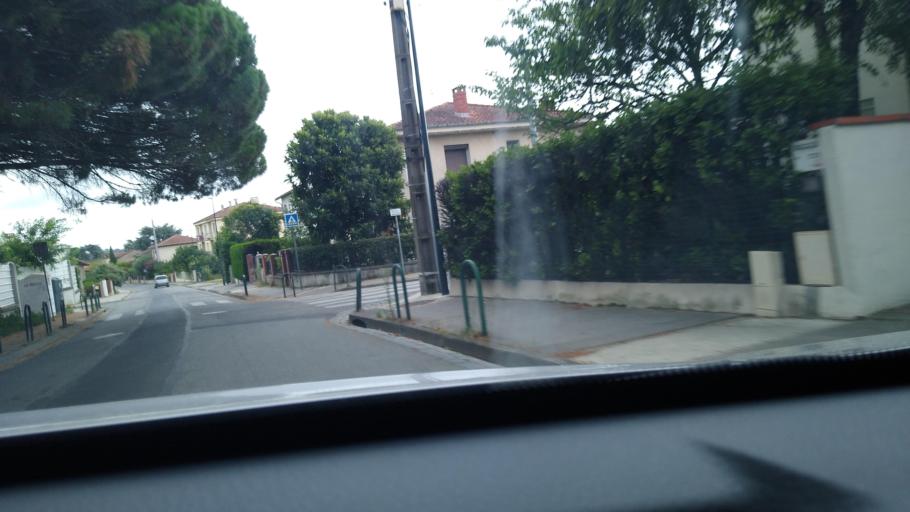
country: FR
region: Midi-Pyrenees
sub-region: Departement de la Haute-Garonne
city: Toulouse
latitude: 43.6141
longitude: 1.4691
